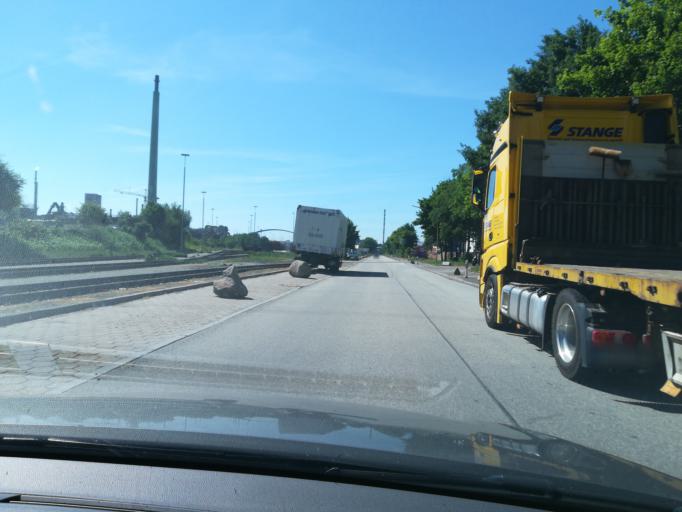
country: DE
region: Hamburg
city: Rothenburgsort
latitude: 53.5131
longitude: 10.0481
